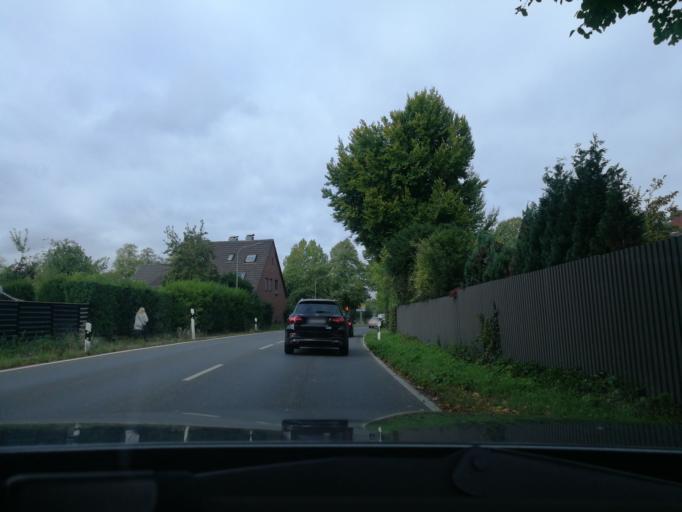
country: DE
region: North Rhine-Westphalia
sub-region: Regierungsbezirk Dusseldorf
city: Neuss
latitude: 51.1587
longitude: 6.7273
